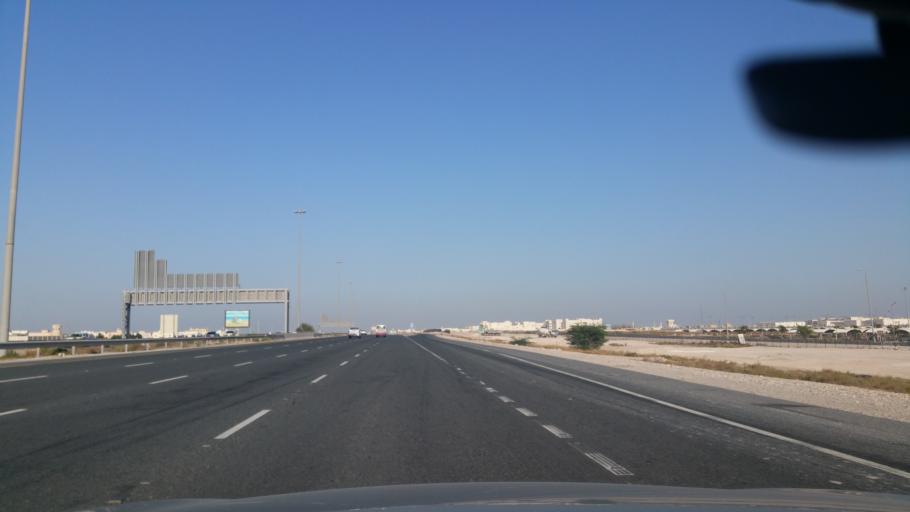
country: QA
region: Baladiyat ar Rayyan
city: Ar Rayyan
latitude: 25.1827
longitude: 51.3560
